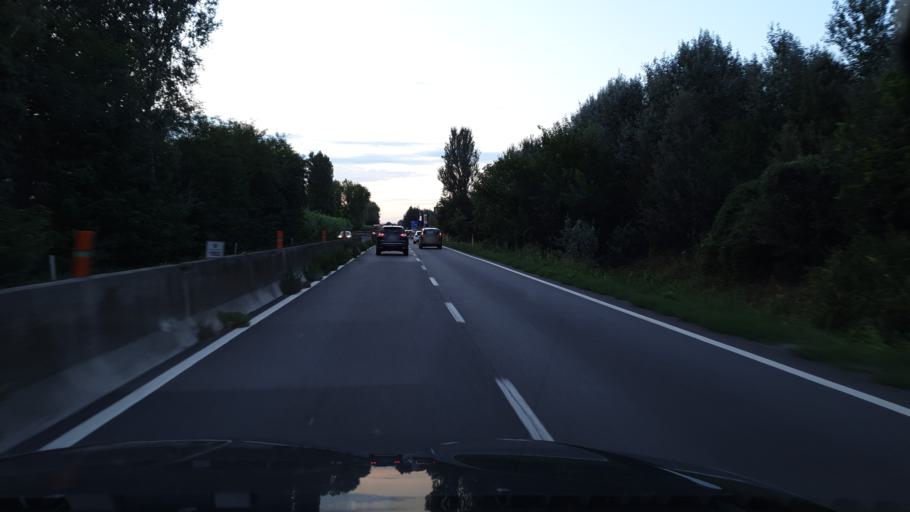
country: IT
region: Emilia-Romagna
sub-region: Provincia di Ravenna
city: Ravenna
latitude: 44.4051
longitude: 12.1767
